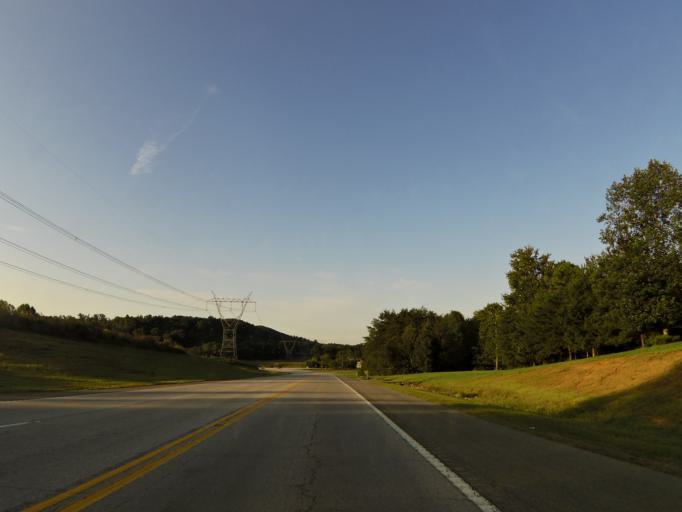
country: US
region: Tennessee
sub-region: Meigs County
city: Decatur
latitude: 35.6021
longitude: -84.6761
